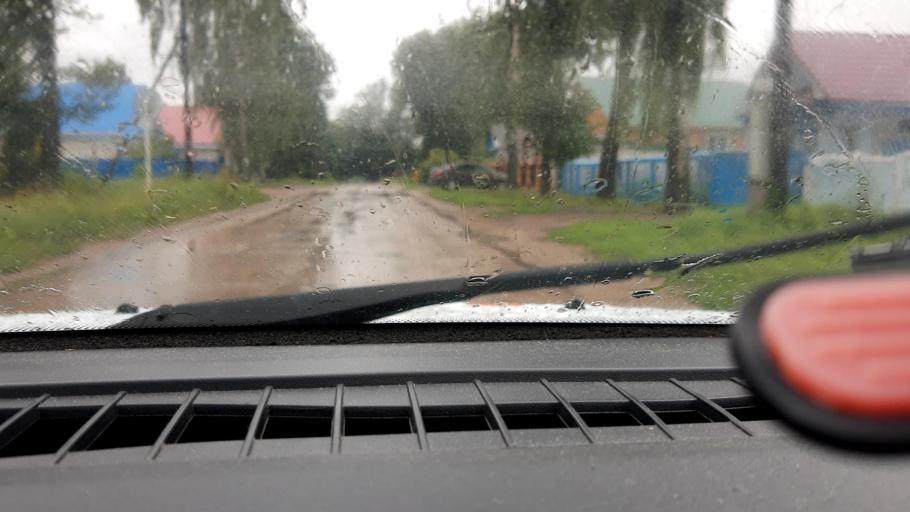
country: RU
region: Nizjnij Novgorod
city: Lyskovo
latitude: 56.0300
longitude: 45.0191
